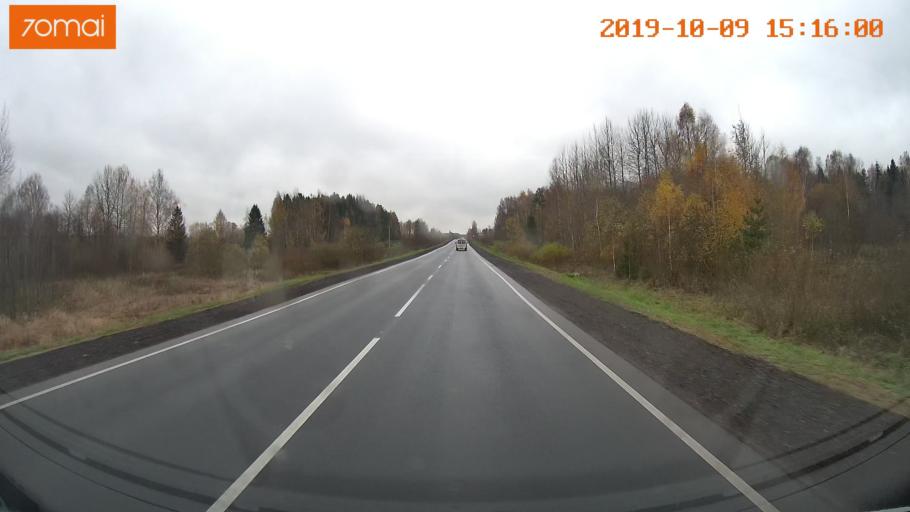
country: RU
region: Kostroma
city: Susanino
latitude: 58.1154
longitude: 41.5875
